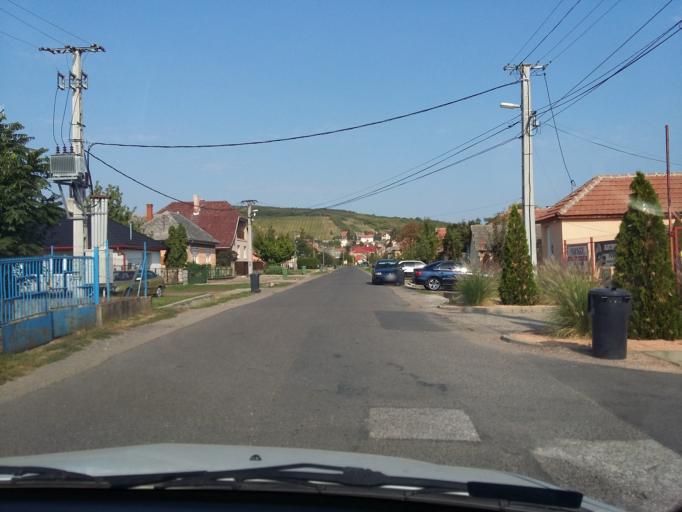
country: HU
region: Borsod-Abauj-Zemplen
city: Bekecs
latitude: 48.1486
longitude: 21.1789
